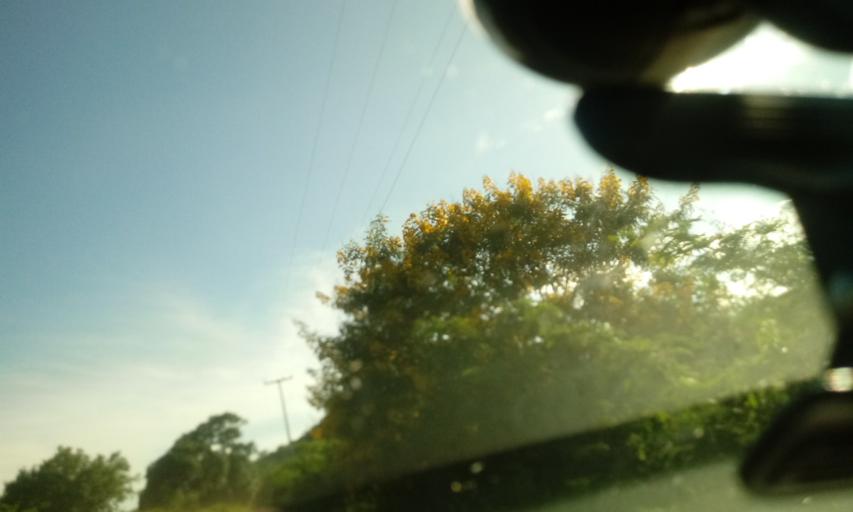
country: BR
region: Bahia
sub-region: Riacho De Santana
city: Riacho de Santana
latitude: -13.8234
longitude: -42.7648
